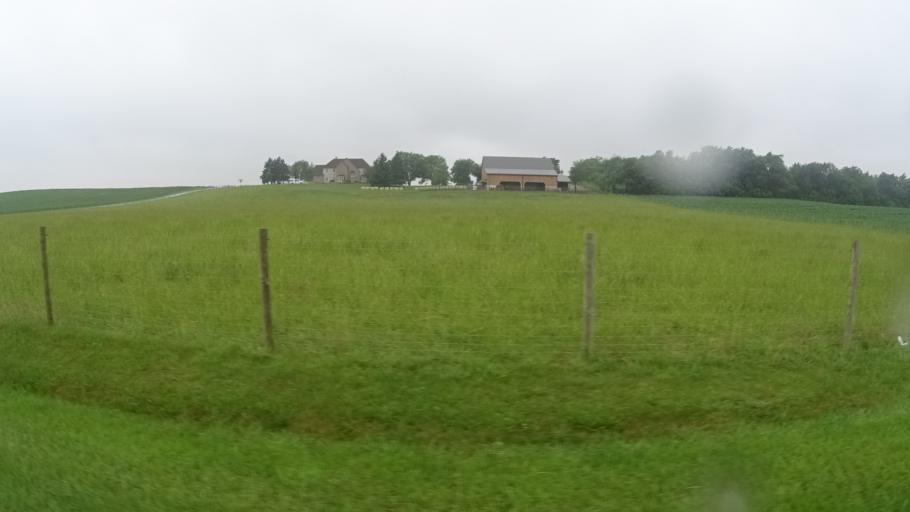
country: US
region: Ohio
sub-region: Huron County
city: Bellevue
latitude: 41.3350
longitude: -82.8434
